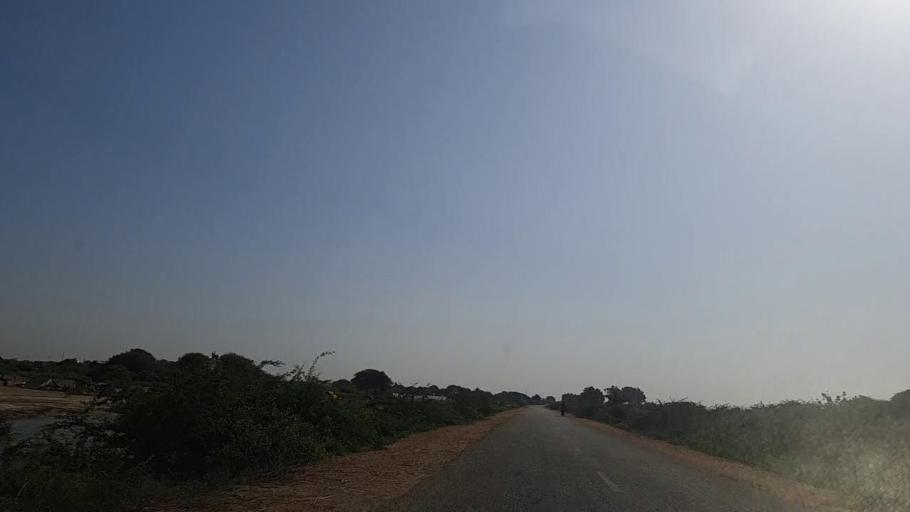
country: PK
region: Sindh
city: Jati
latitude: 24.4286
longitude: 68.2586
